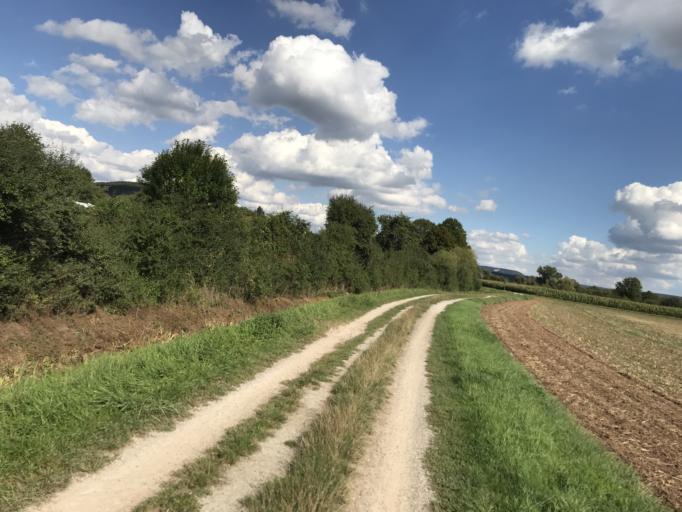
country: DE
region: Hesse
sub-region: Regierungsbezirk Kassel
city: Eschwege
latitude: 51.2029
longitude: 10.0433
